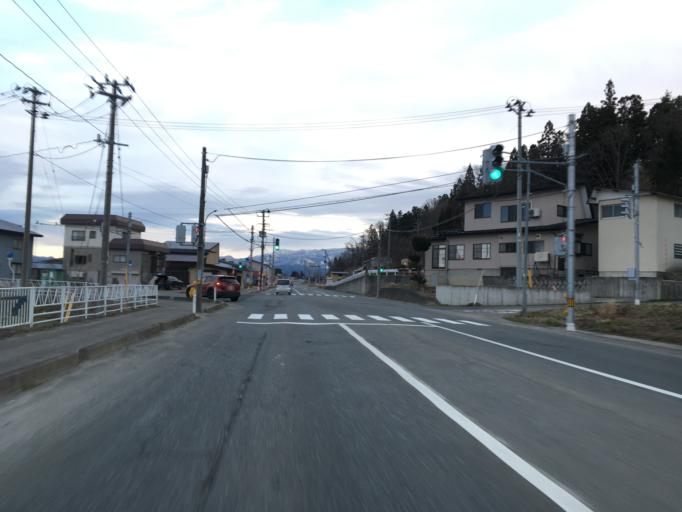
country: JP
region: Yamagata
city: Yonezawa
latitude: 37.9452
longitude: 140.0734
